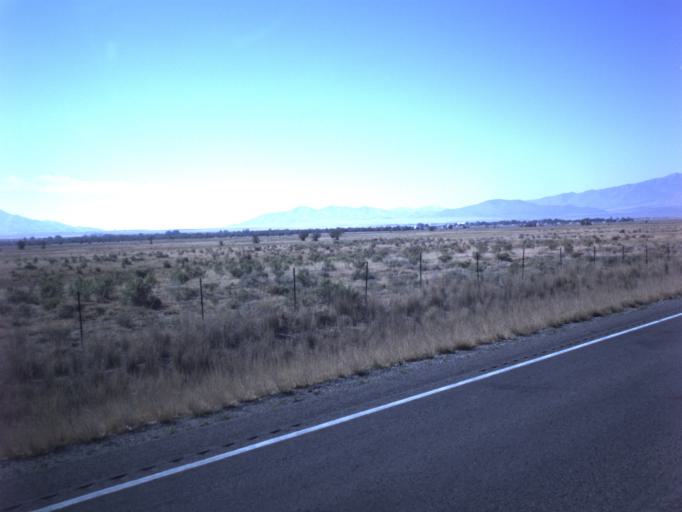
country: US
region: Utah
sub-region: Tooele County
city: Erda
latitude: 40.6324
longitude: -112.3358
